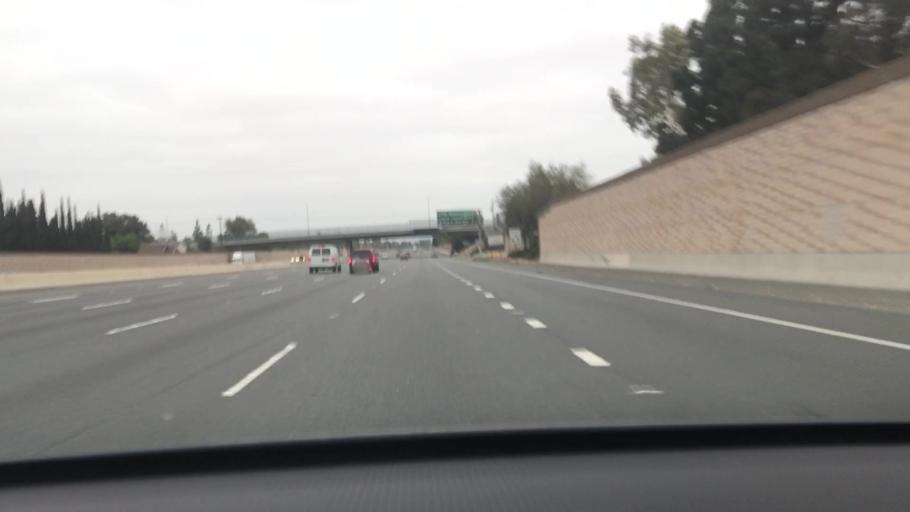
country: US
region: California
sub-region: Orange County
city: Tustin
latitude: 33.7697
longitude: -117.8312
